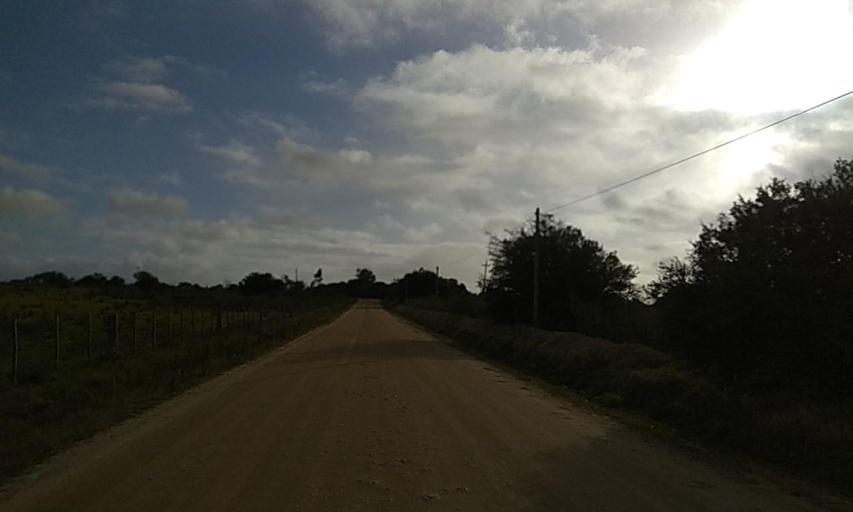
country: UY
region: Florida
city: Florida
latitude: -34.0566
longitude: -56.1907
